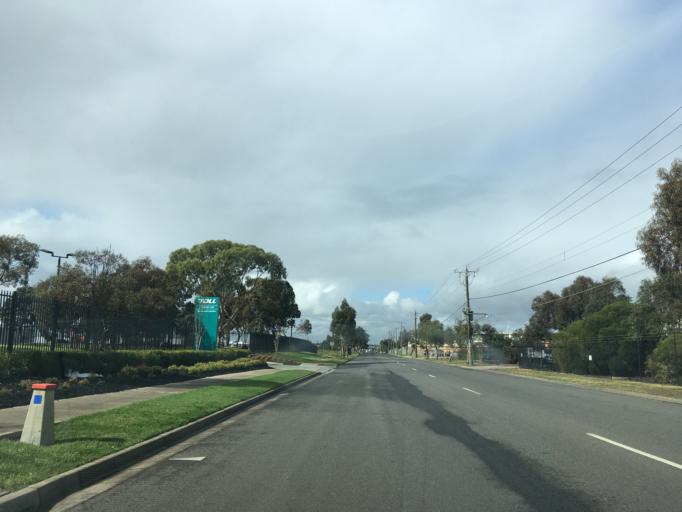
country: AU
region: Victoria
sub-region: Hobsons Bay
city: Laverton
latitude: -37.8369
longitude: 144.7971
